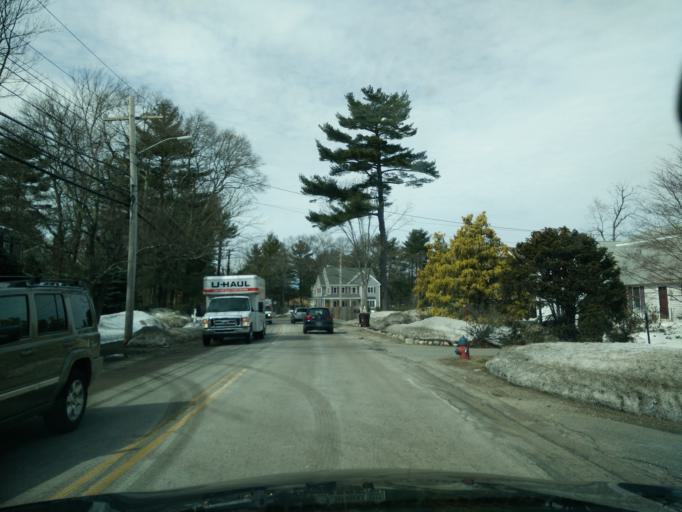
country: US
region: Massachusetts
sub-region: Norfolk County
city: Walpole
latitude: 42.1443
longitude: -71.2256
